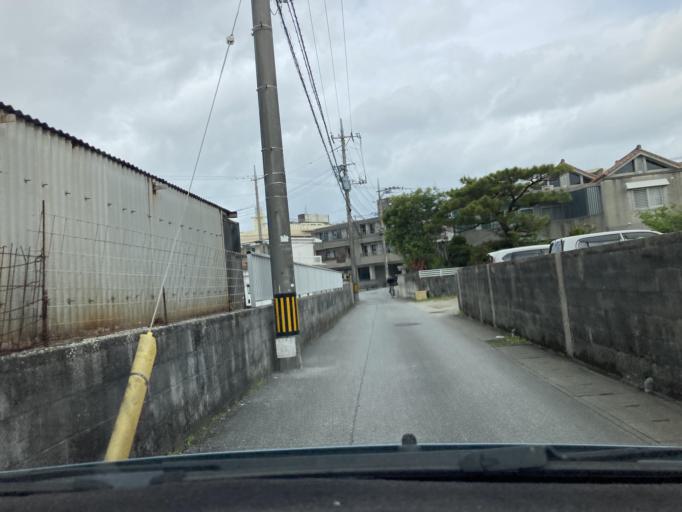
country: JP
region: Okinawa
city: Ginowan
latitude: 26.2370
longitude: 127.7376
